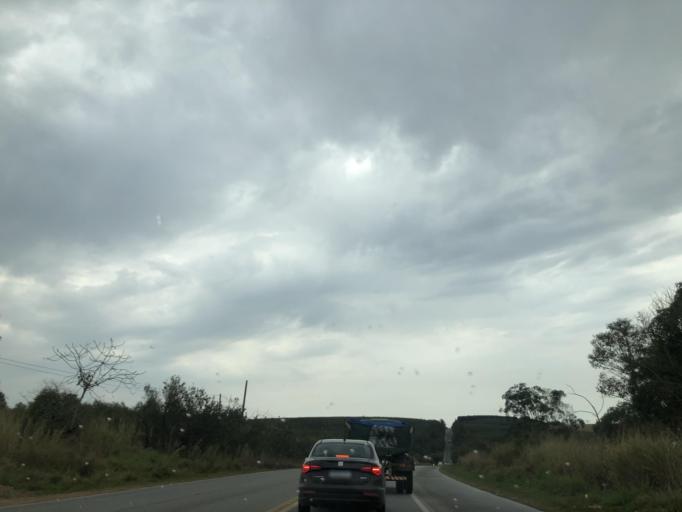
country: BR
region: Sao Paulo
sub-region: Salto De Pirapora
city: Salto de Pirapora
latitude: -23.6847
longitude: -47.6065
